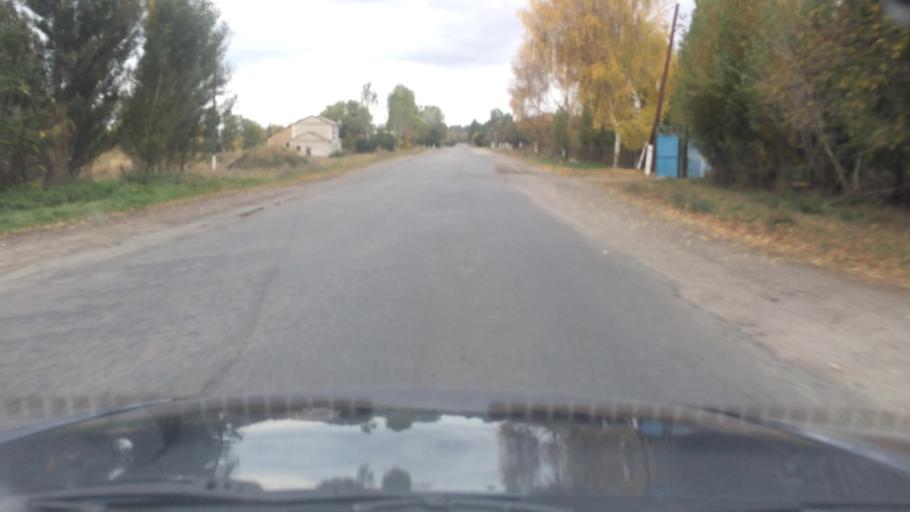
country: KG
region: Ysyk-Koel
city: Tyup
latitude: 42.7562
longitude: 78.1440
